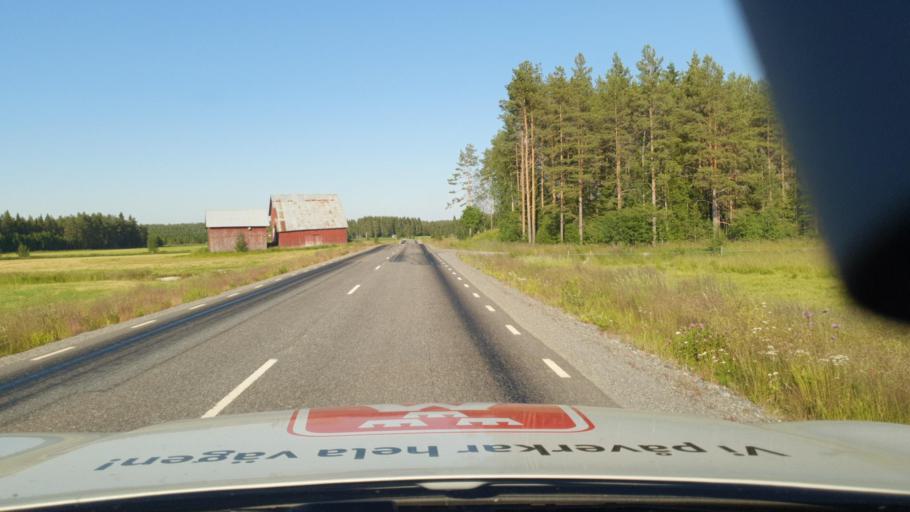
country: SE
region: Vaesterbotten
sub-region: Robertsfors Kommun
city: Robertsfors
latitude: 64.2324
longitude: 20.9600
